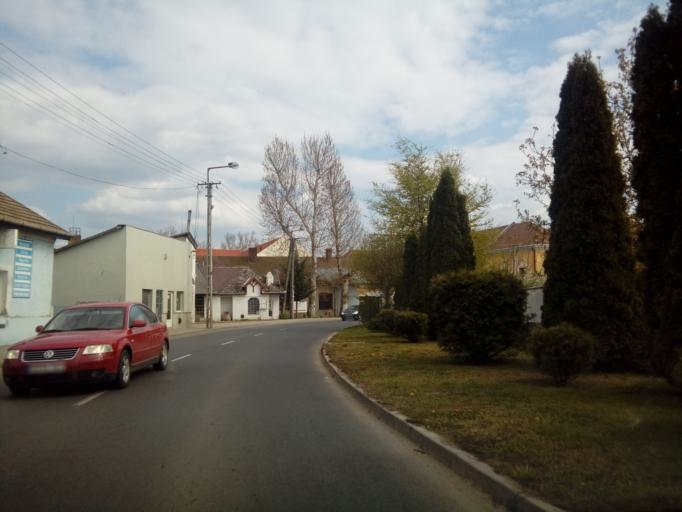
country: HU
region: Szabolcs-Szatmar-Bereg
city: Nagykallo
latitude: 47.8761
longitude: 21.8436
